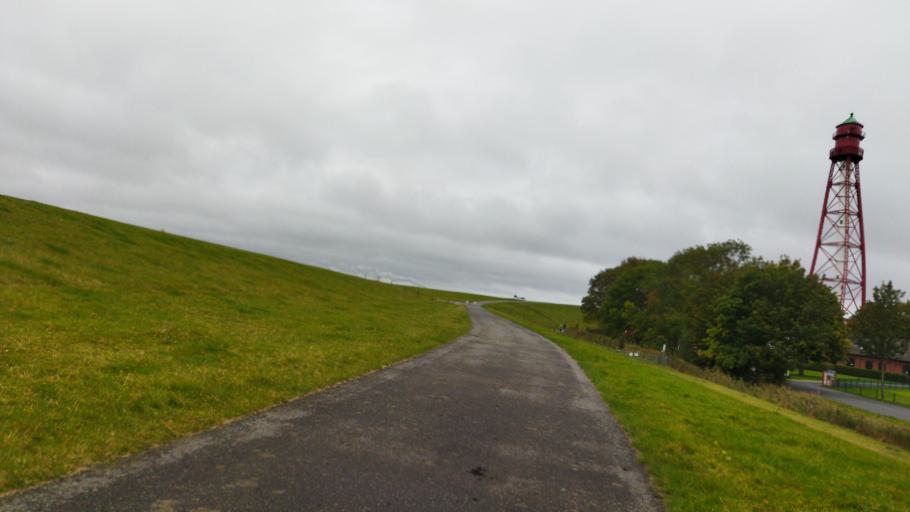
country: NL
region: Groningen
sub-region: Gemeente Delfzijl
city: Delfzijl
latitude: 53.4043
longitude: 7.0175
